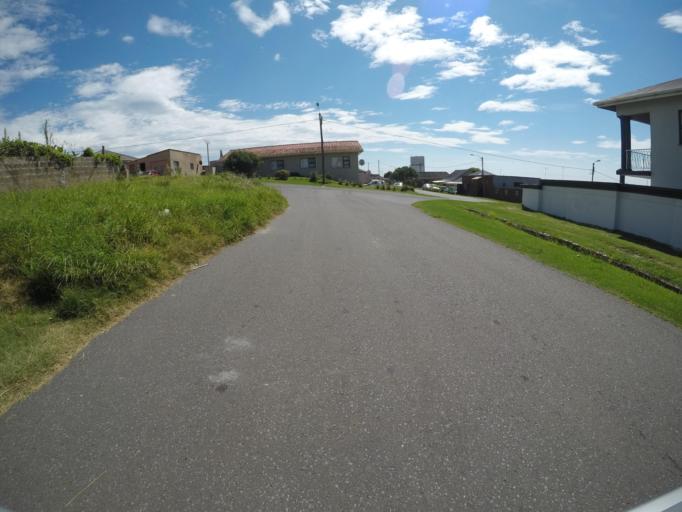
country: ZA
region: Eastern Cape
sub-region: Buffalo City Metropolitan Municipality
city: East London
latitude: -33.0355
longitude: 27.9070
